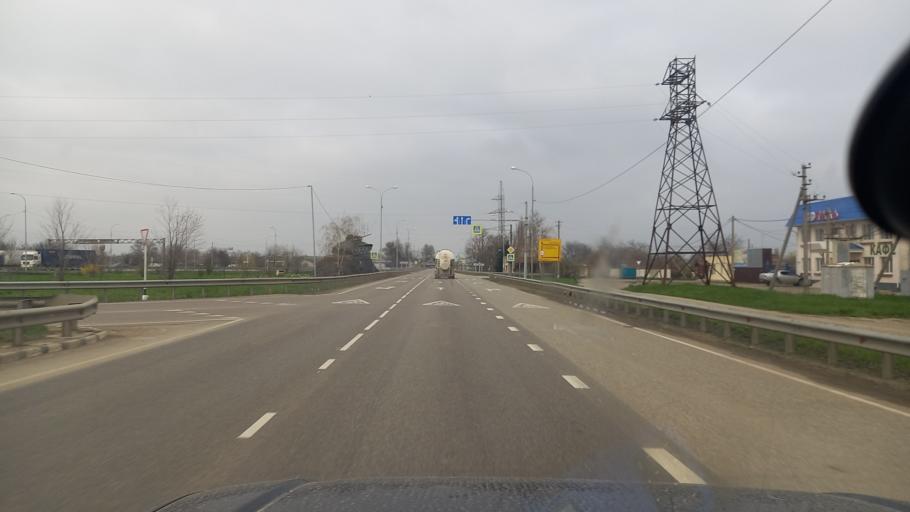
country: RU
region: Krasnodarskiy
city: Trudobelikovskiy
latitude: 45.2821
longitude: 38.2407
